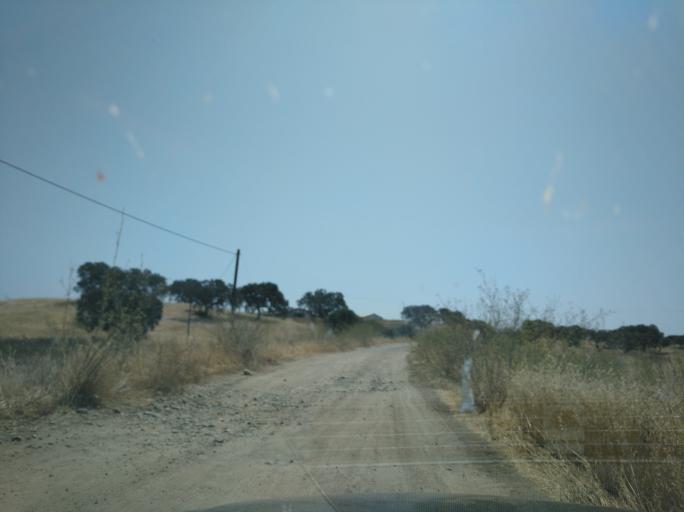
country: PT
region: Portalegre
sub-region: Campo Maior
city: Campo Maior
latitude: 39.0310
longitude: -6.9802
